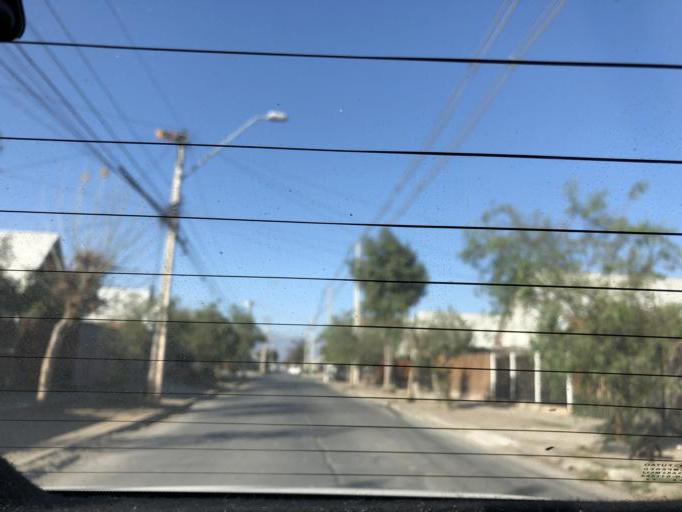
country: CL
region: Santiago Metropolitan
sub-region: Provincia de Cordillera
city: Puente Alto
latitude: -33.6184
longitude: -70.5932
